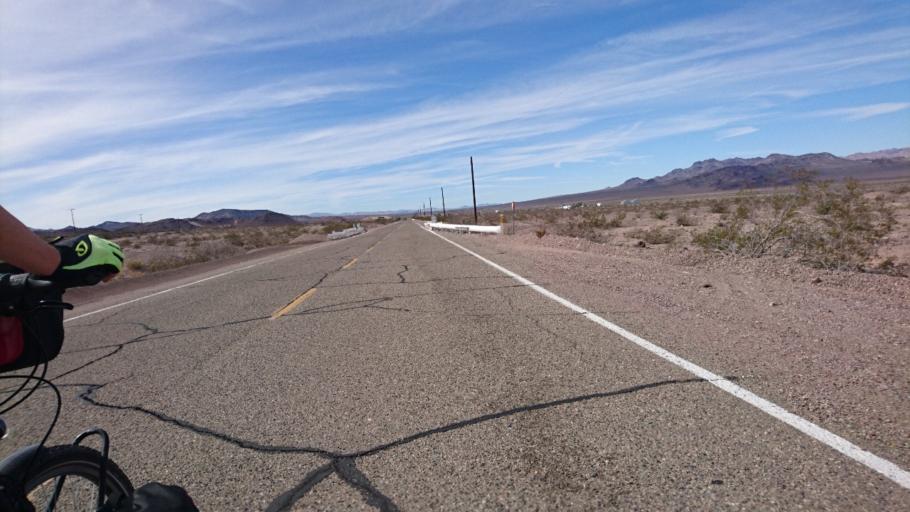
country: US
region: California
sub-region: San Bernardino County
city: Twentynine Palms
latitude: 34.7242
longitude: -116.1484
